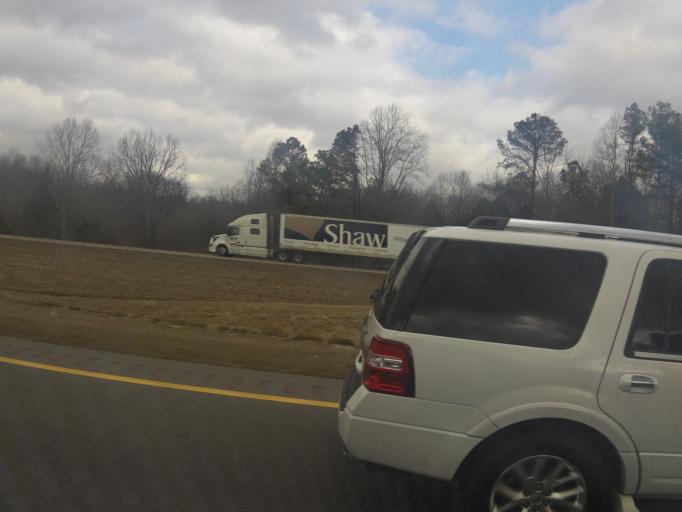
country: US
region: Tennessee
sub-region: Coffee County
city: New Union
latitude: 35.5391
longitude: -86.1731
